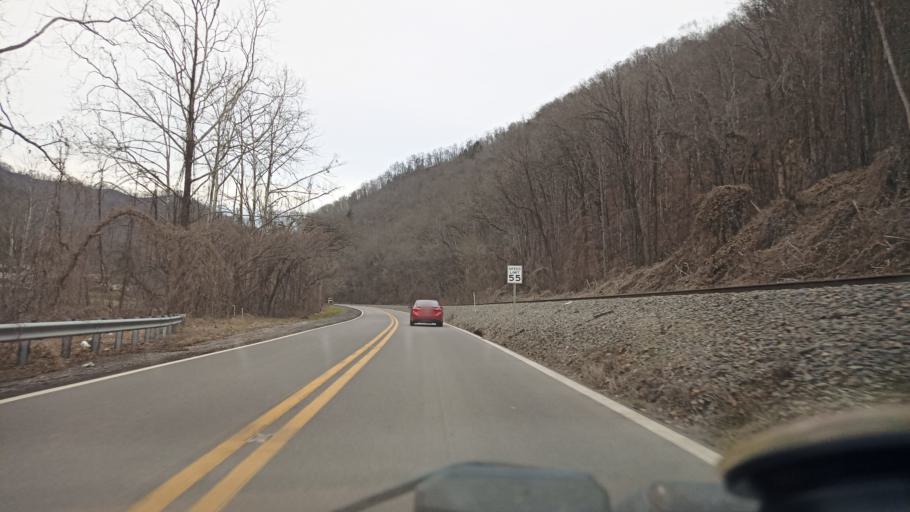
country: US
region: West Virginia
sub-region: Logan County
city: Mallory
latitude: 37.7176
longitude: -81.8683
